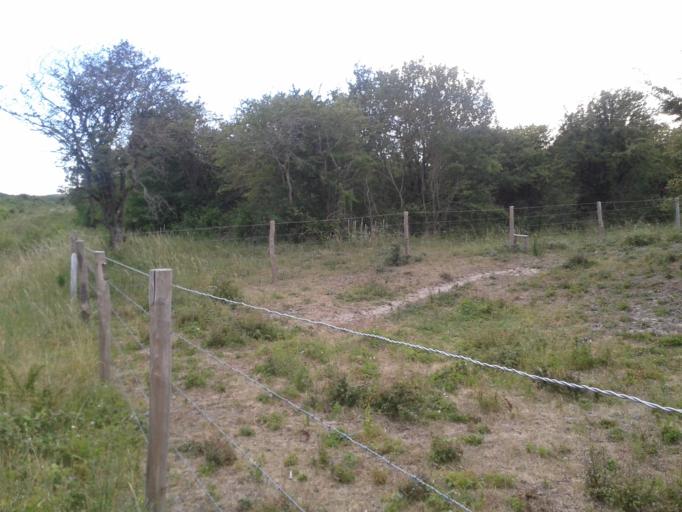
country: FR
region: Picardie
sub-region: Departement de la Somme
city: Fort-Mahon-Plage
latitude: 50.3563
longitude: 1.5629
